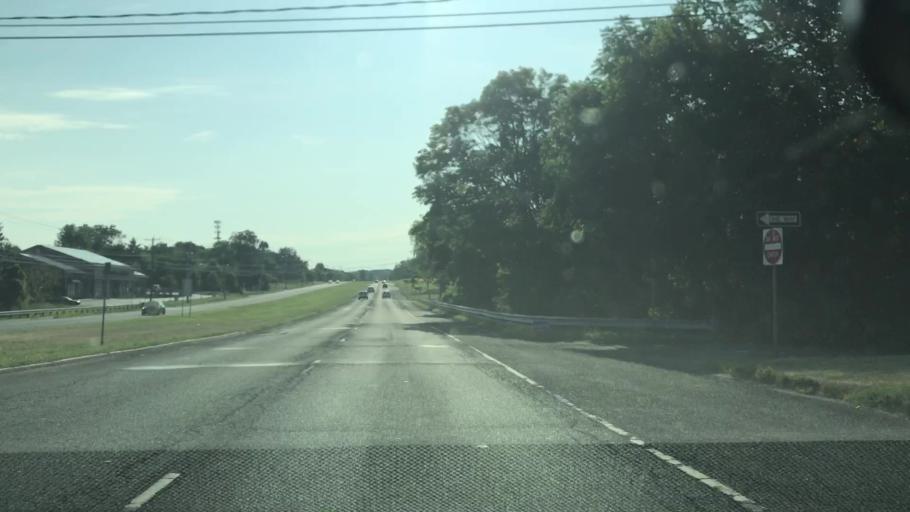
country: US
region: New Jersey
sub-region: Hunterdon County
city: Lebanon
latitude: 40.6440
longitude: -74.8257
